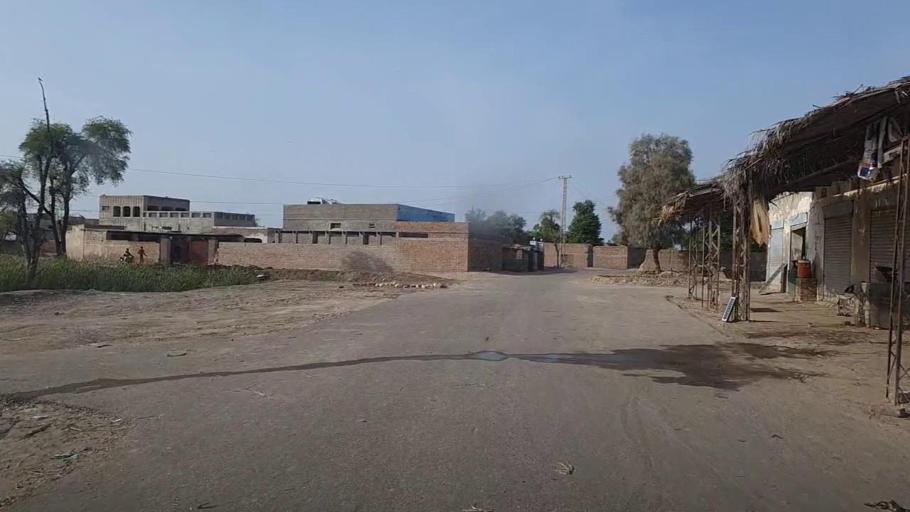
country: PK
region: Sindh
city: Ubauro
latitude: 28.1032
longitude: 69.8454
